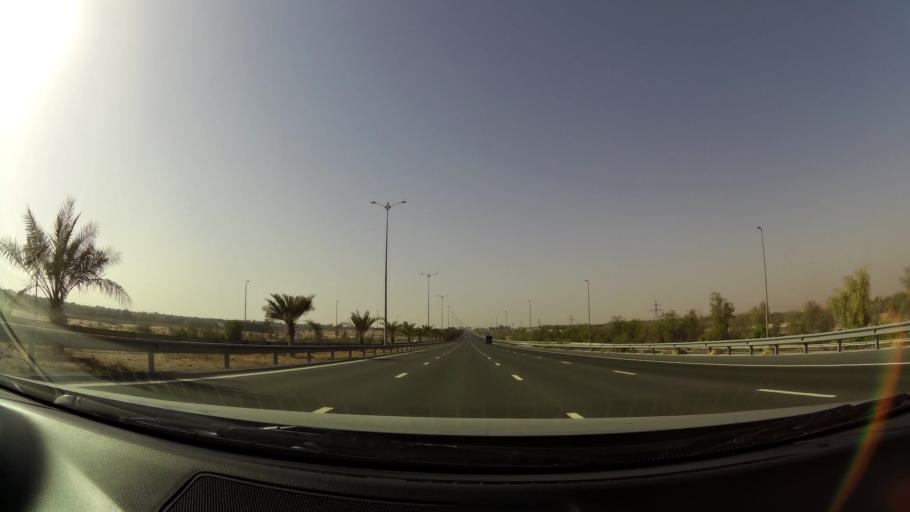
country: OM
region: Al Buraimi
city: Al Buraymi
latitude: 24.5704
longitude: 55.7476
